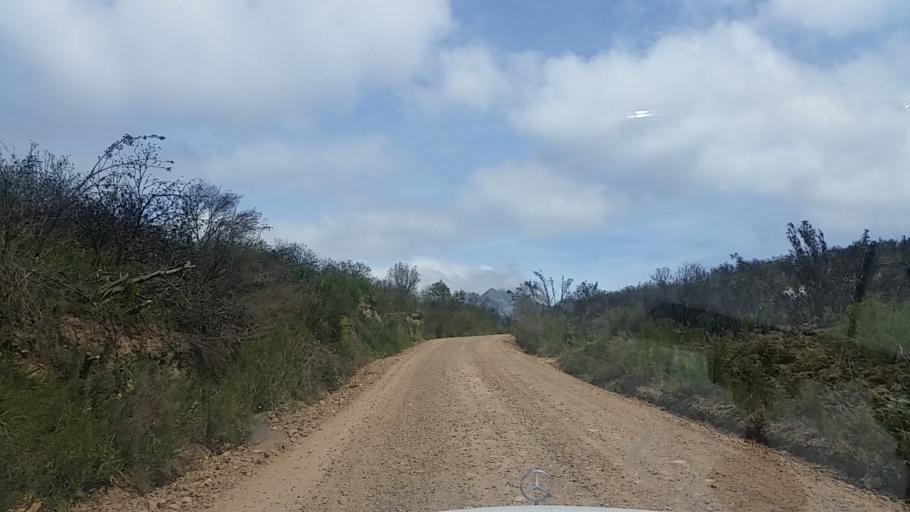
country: ZA
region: Western Cape
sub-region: Eden District Municipality
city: George
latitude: -33.8829
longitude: 22.4325
